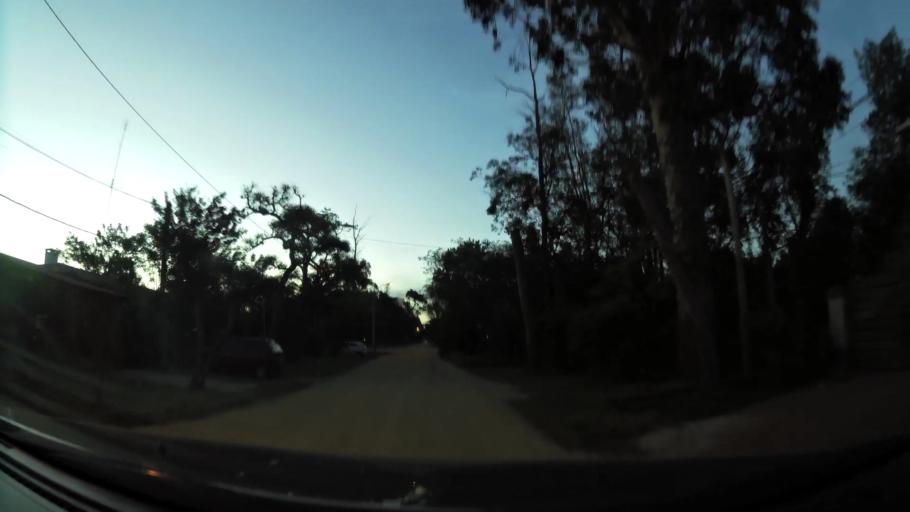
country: UY
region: Canelones
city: Atlantida
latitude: -34.7679
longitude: -55.7558
